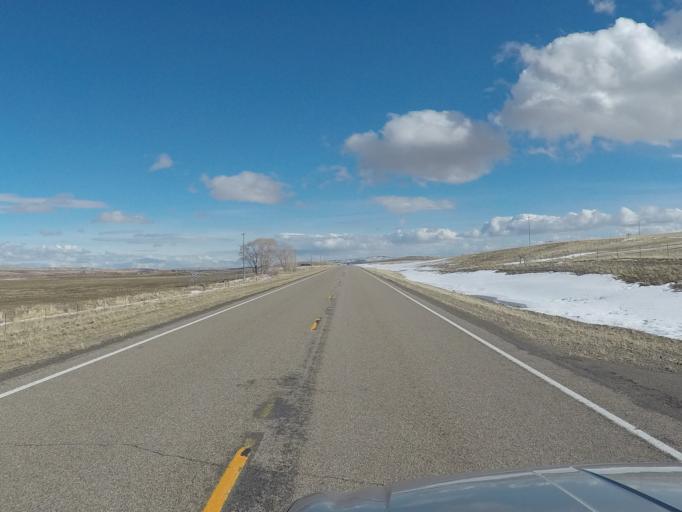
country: US
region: Montana
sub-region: Meagher County
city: White Sulphur Springs
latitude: 46.5326
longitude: -110.4284
